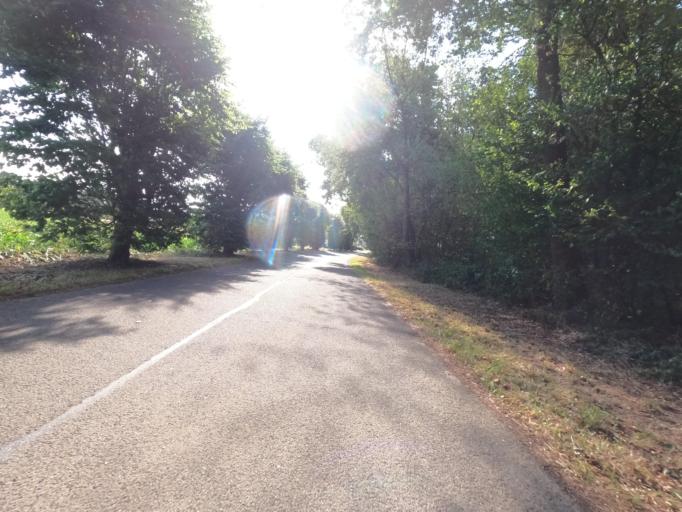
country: DE
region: North Rhine-Westphalia
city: Huckelhoven
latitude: 51.1000
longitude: 6.2088
